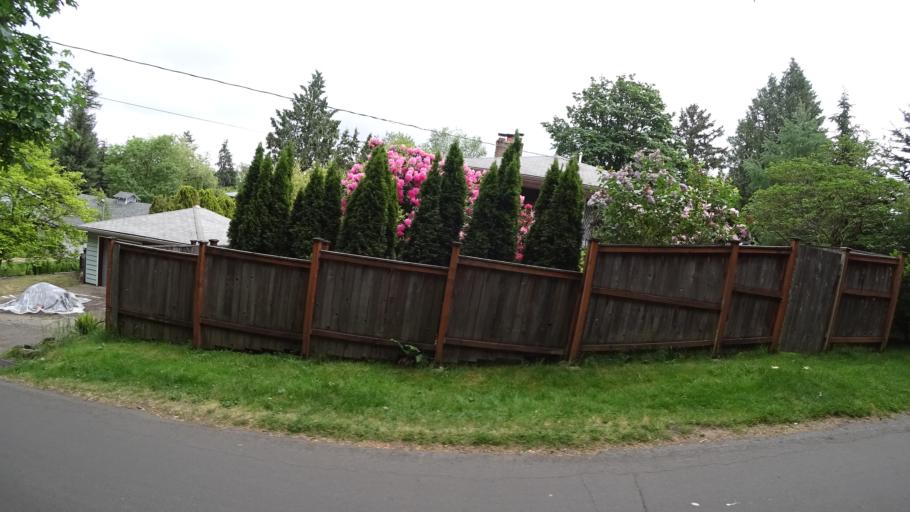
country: US
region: Oregon
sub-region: Washington County
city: Garden Home-Whitford
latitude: 45.4741
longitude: -122.7387
